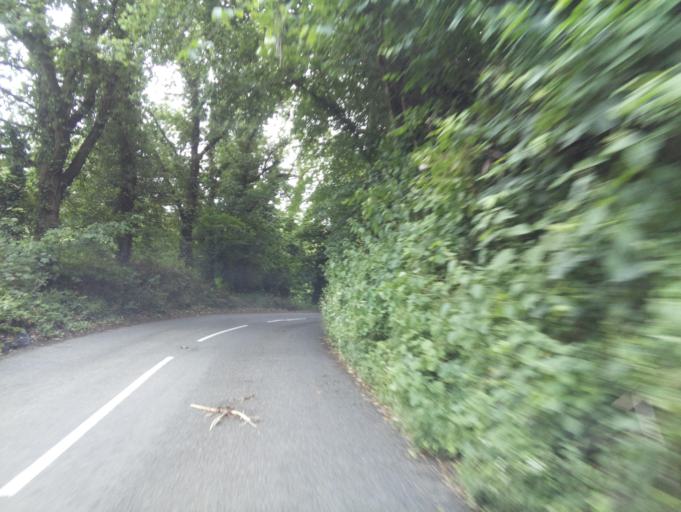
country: GB
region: England
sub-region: Devon
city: Chudleigh
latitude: 50.6499
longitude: -3.6415
